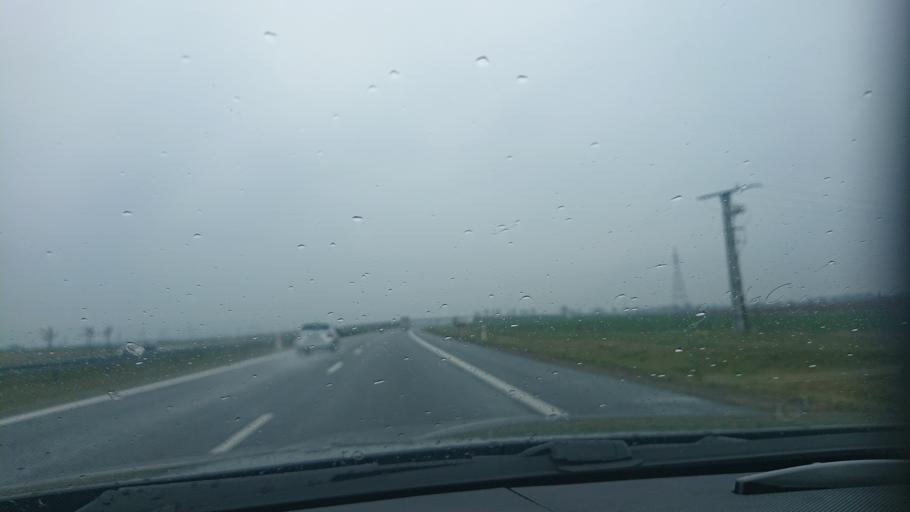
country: PL
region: Greater Poland Voivodeship
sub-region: Powiat gnieznienski
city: Gniezno
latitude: 52.5659
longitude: 17.5619
